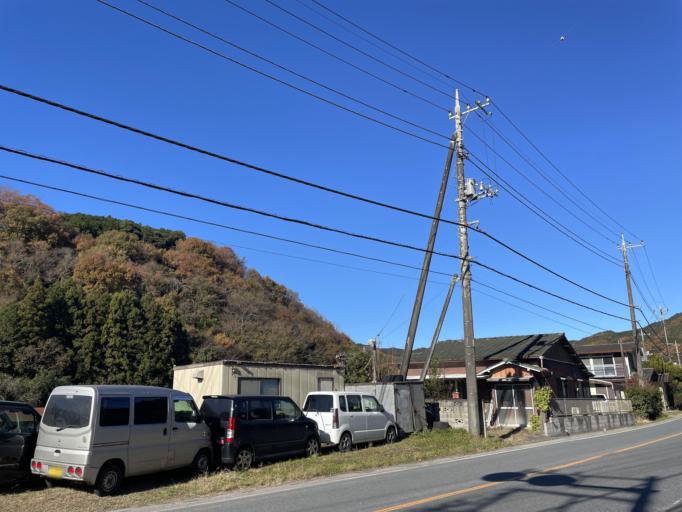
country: JP
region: Saitama
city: Ogawa
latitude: 36.0451
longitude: 139.2288
